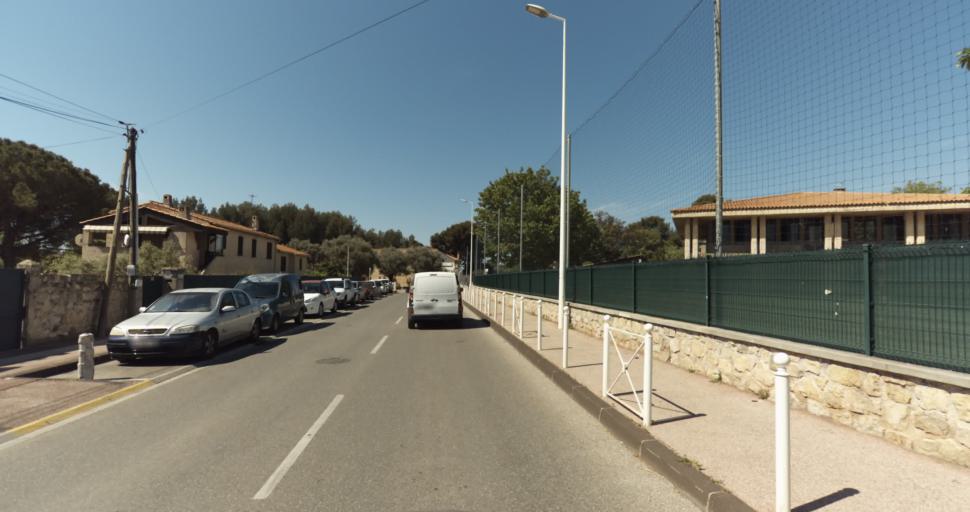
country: FR
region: Provence-Alpes-Cote d'Azur
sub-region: Departement du Var
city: Le Revest-les-Eaux
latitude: 43.1469
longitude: 5.9012
